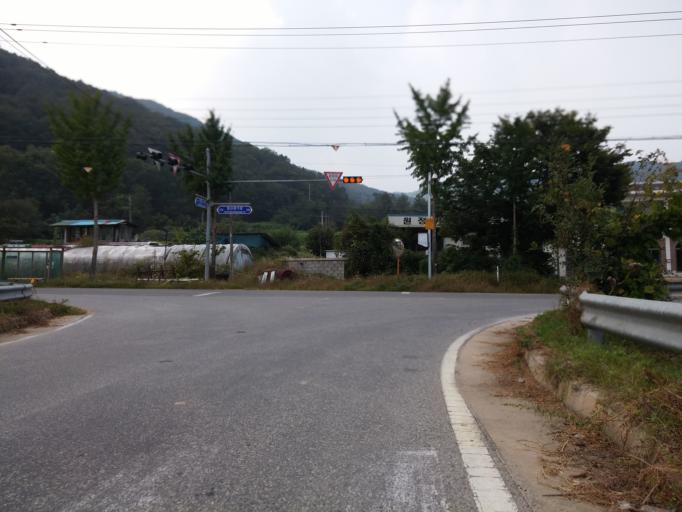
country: KR
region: Chungcheongbuk-do
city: Yong-dong
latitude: 36.3890
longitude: 127.8142
